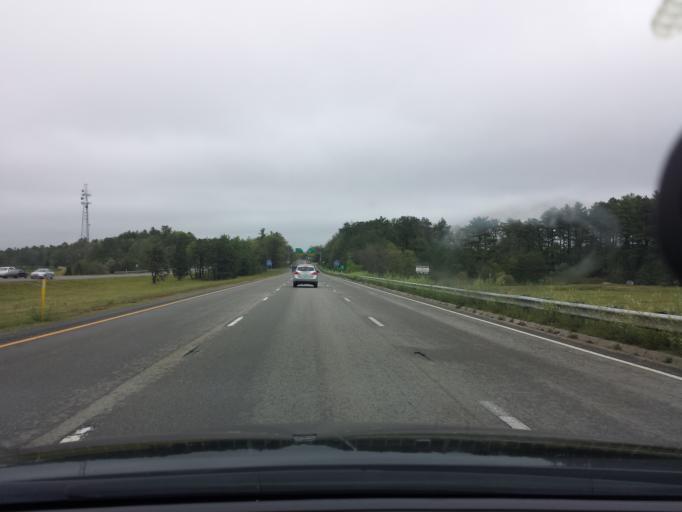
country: US
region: Massachusetts
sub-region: Plymouth County
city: Wareham Center
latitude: 41.7786
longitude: -70.7363
